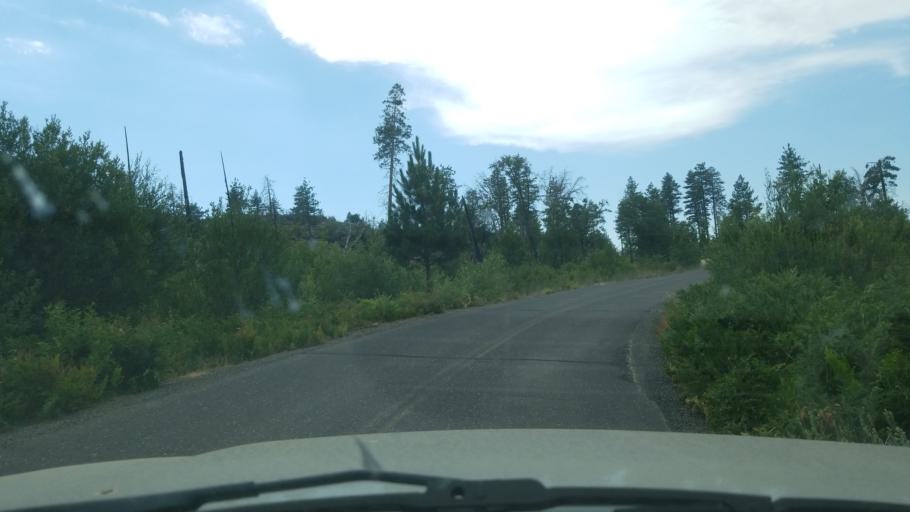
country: US
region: California
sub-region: Mariposa County
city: Yosemite Valley
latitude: 37.9023
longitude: -119.8116
